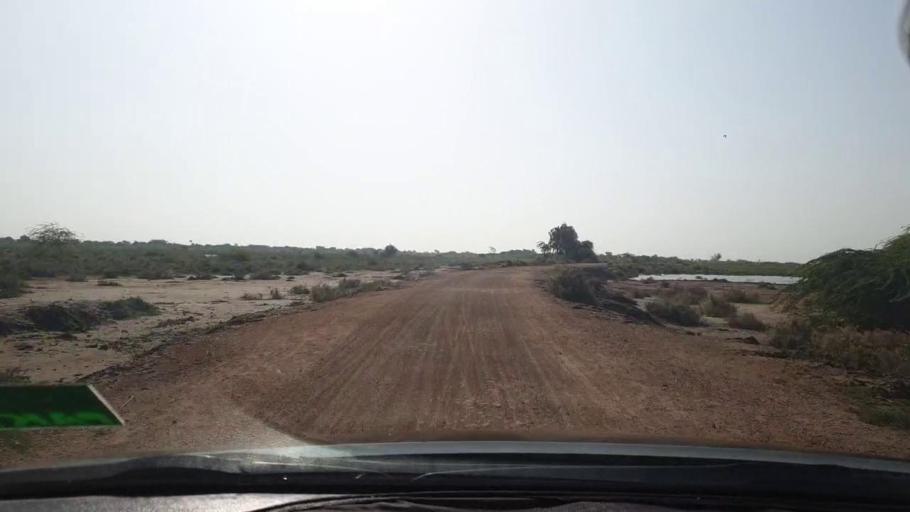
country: PK
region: Sindh
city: Tando Bago
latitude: 24.7174
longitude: 68.9685
